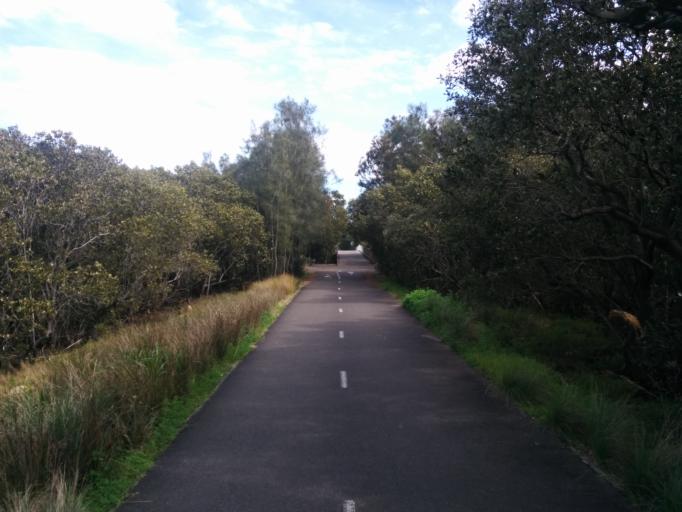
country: AU
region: New South Wales
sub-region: Canada Bay
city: Concord West
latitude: -33.8446
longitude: 151.0811
